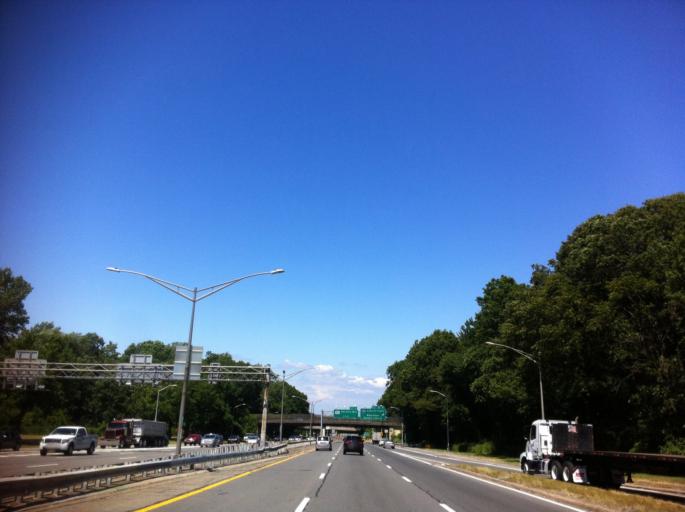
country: US
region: New York
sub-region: Nassau County
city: Bellerose Terrace
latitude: 40.7340
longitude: -73.7450
